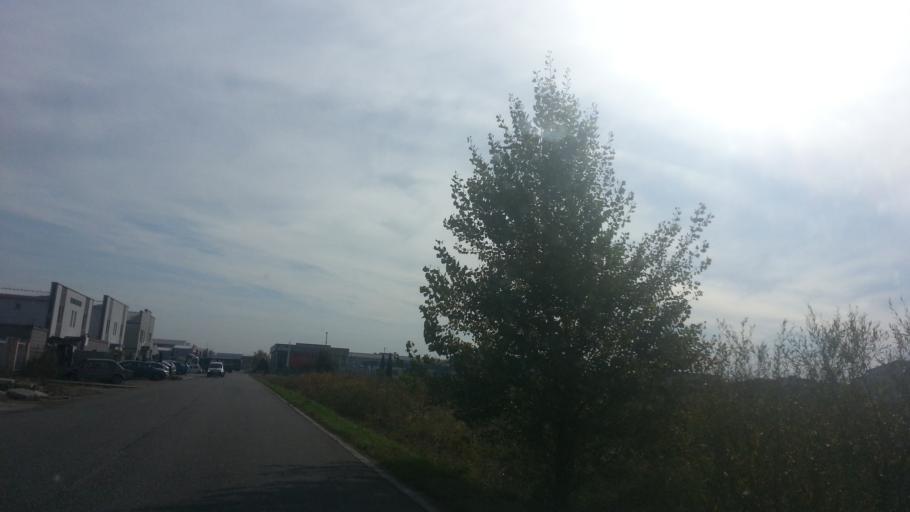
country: RS
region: Autonomna Pokrajina Vojvodina
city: Nova Pazova
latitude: 44.9519
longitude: 20.1959
